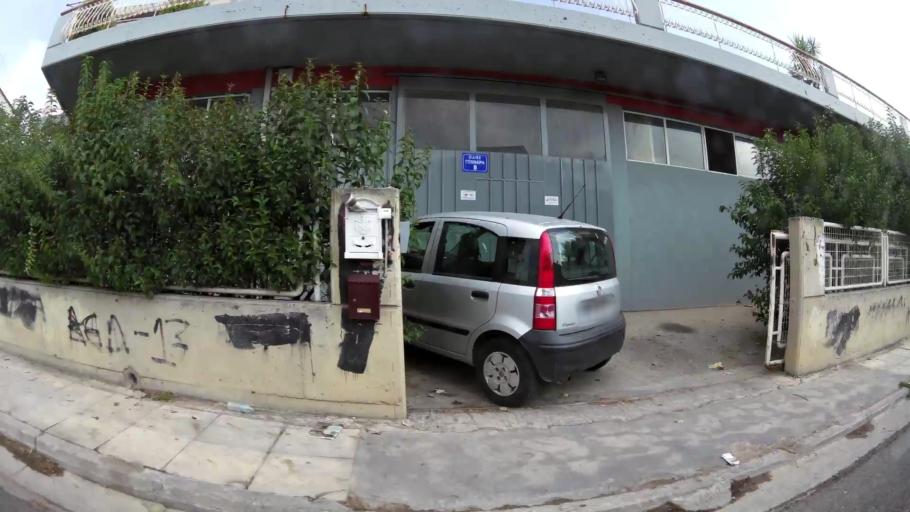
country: GR
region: Attica
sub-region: Nomarchia Athinas
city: Nea Filadelfeia
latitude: 38.0492
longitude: 23.7282
